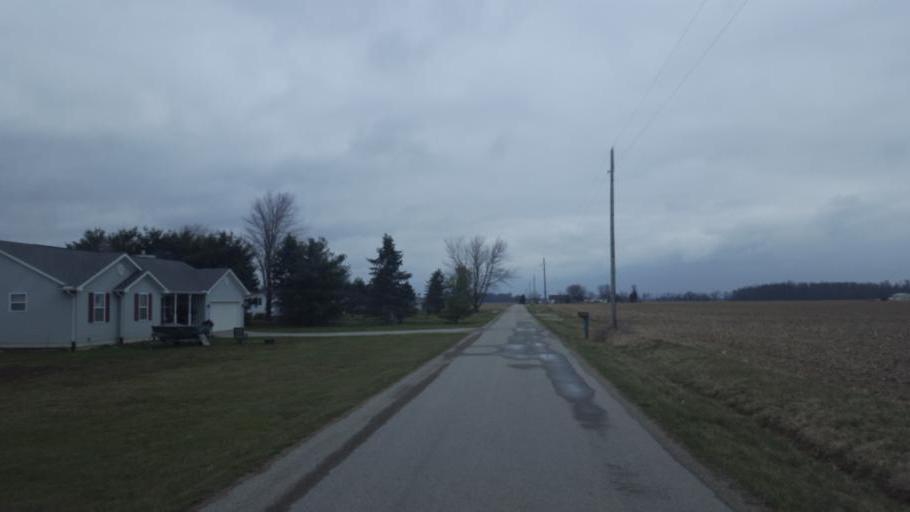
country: US
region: Ohio
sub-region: Delaware County
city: Ashley
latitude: 40.4668
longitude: -82.9884
